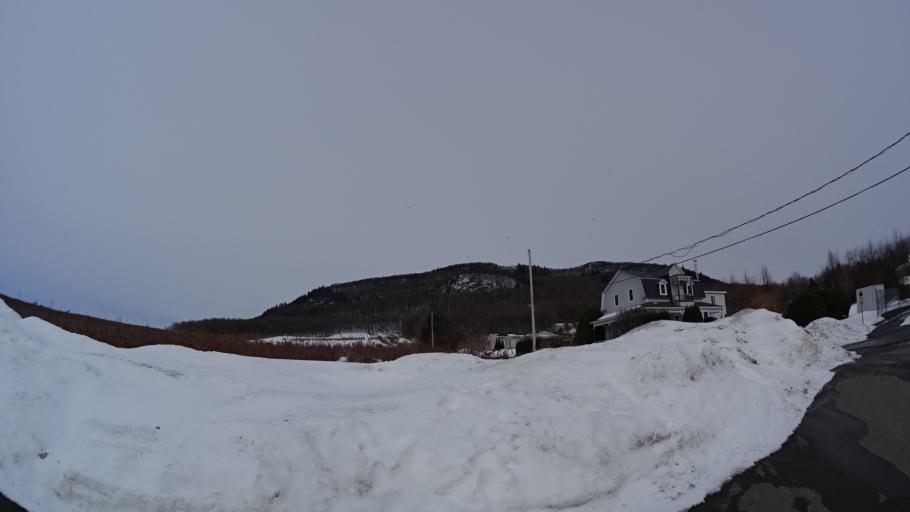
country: CA
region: Quebec
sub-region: Monteregie
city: Saint-Pie
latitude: 45.4381
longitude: -72.8807
